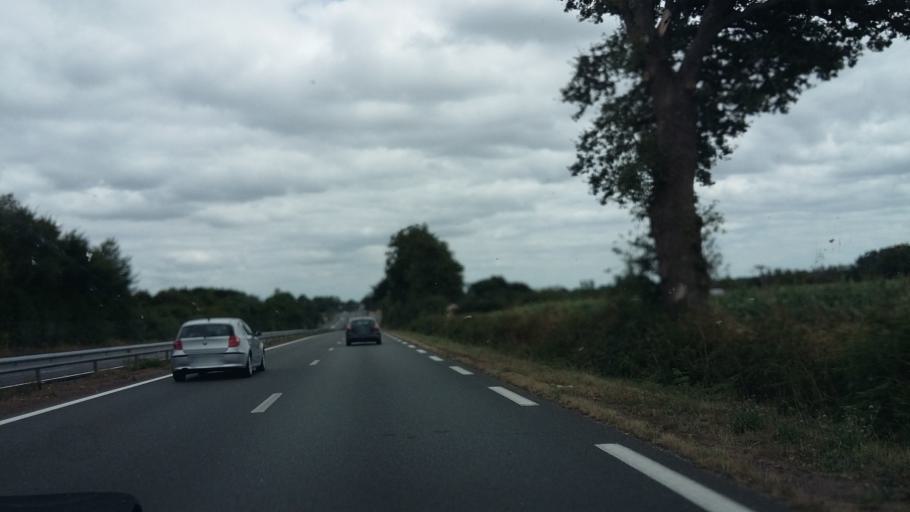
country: FR
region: Pays de la Loire
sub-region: Departement de la Vendee
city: Venansault
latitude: 46.7042
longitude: -1.5062
